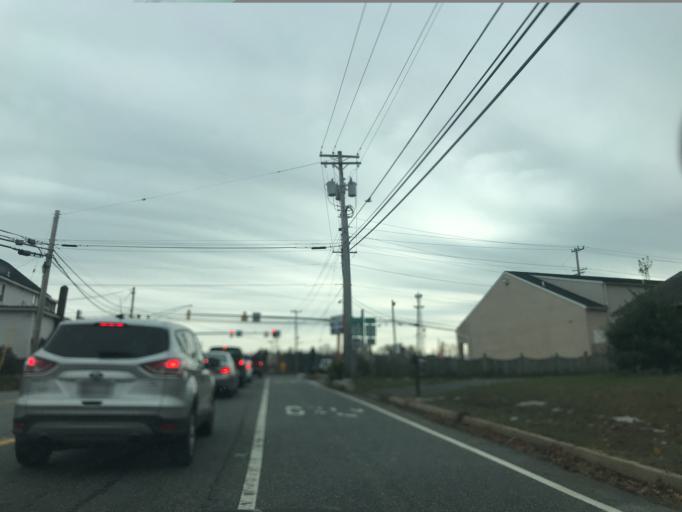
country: US
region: Maryland
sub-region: Harford County
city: Bel Air North
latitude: 39.5792
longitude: -76.3454
